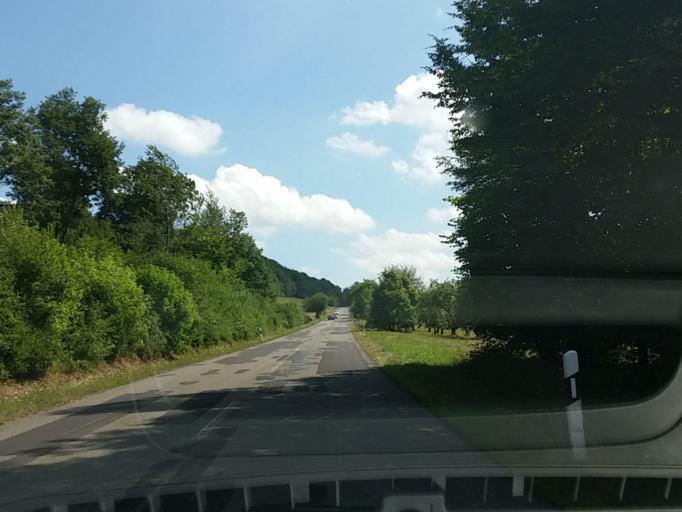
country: DE
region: Saarland
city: Lebach
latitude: 49.4487
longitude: 6.9151
